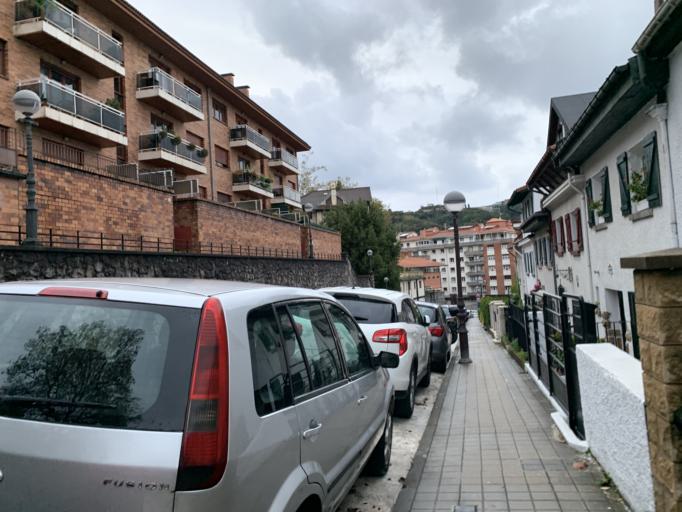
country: ES
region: Basque Country
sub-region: Provincia de Guipuzcoa
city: San Sebastian
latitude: 43.3116
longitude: -2.0012
